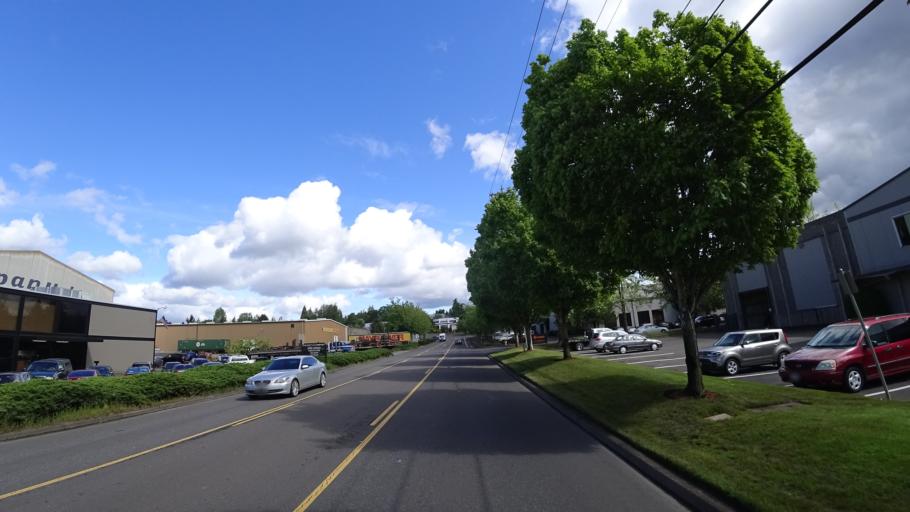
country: US
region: Oregon
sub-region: Washington County
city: Durham
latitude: 45.4166
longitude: -122.7491
